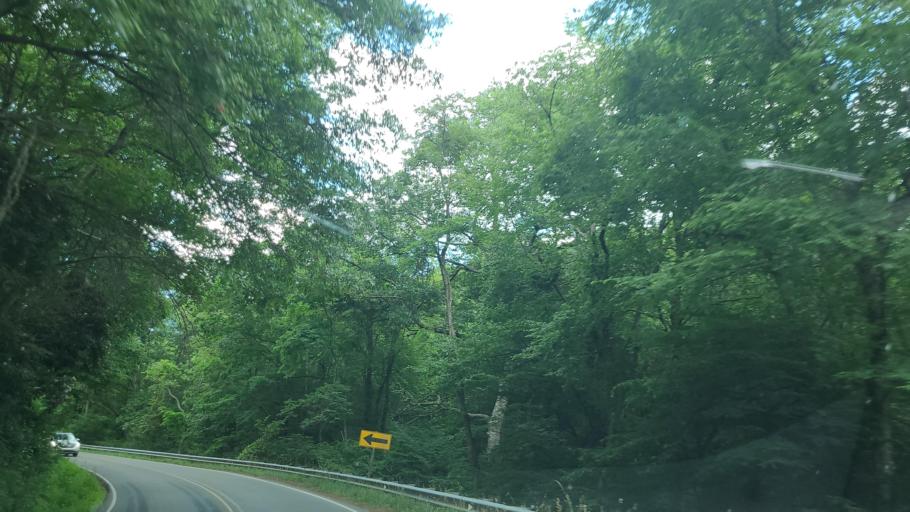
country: US
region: North Carolina
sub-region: Ashe County
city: Jefferson
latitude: 36.3908
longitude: -81.3651
